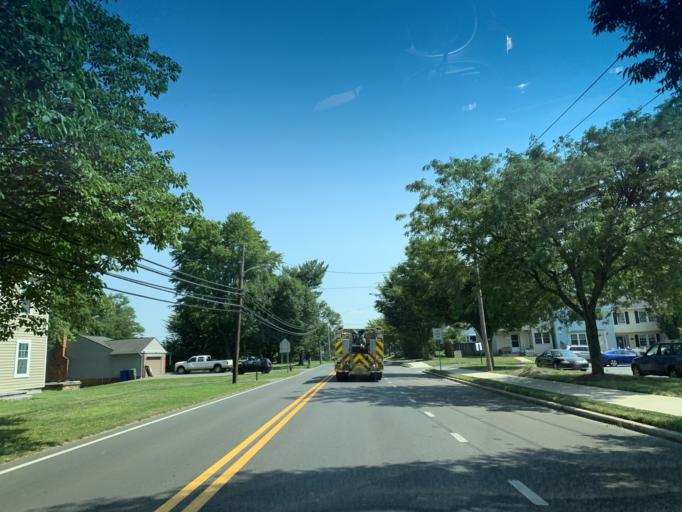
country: US
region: Maryland
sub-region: Montgomery County
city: Poolesville
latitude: 39.1417
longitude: -77.4074
